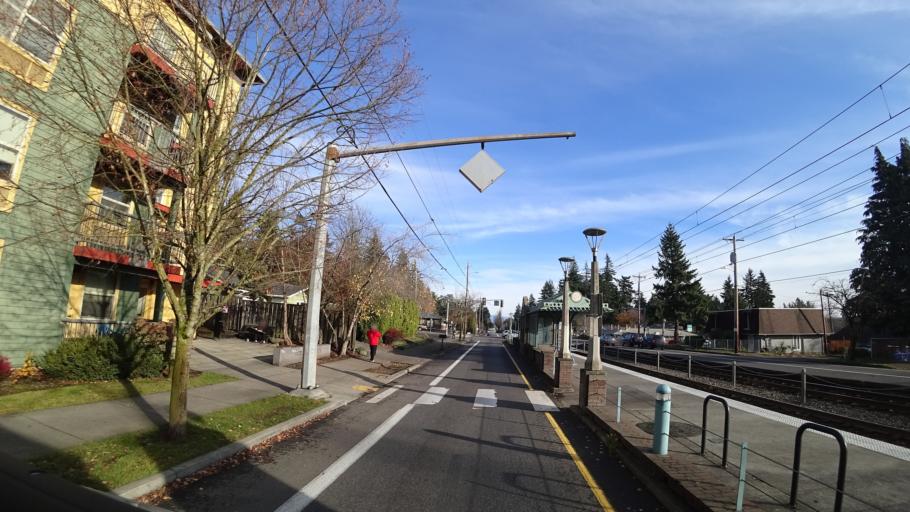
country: US
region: Oregon
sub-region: Multnomah County
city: Lents
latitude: 45.5224
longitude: -122.5115
